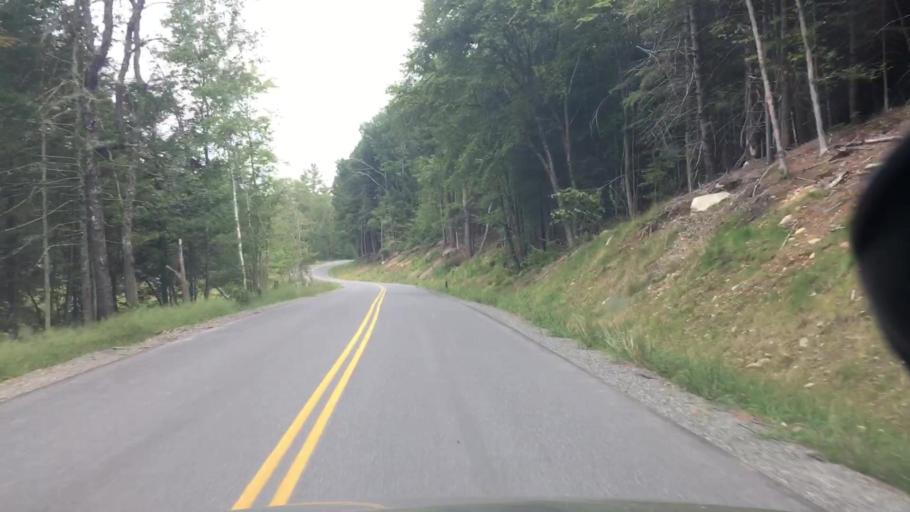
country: US
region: Massachusetts
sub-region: Franklin County
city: Colrain
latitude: 42.7771
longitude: -72.7675
